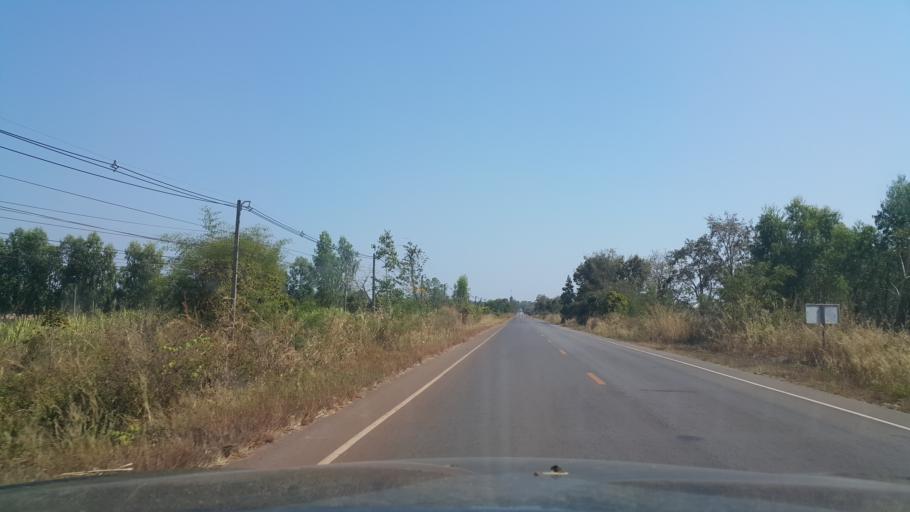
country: TH
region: Changwat Udon Thani
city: Ban Dung
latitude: 17.6088
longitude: 103.2802
